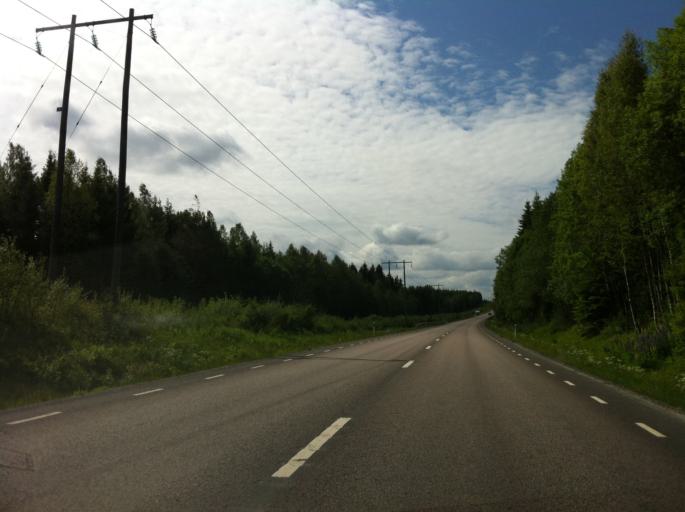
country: SE
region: Vaermland
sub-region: Karlstads Kommun
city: Edsvalla
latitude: 59.4291
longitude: 13.1976
